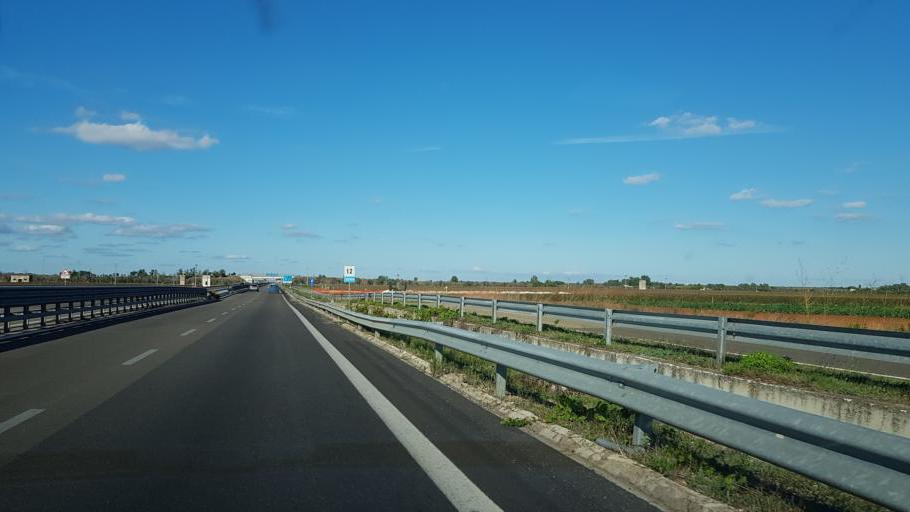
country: IT
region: Apulia
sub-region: Provincia di Lecce
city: Collemeto
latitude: 40.2515
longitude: 18.1160
